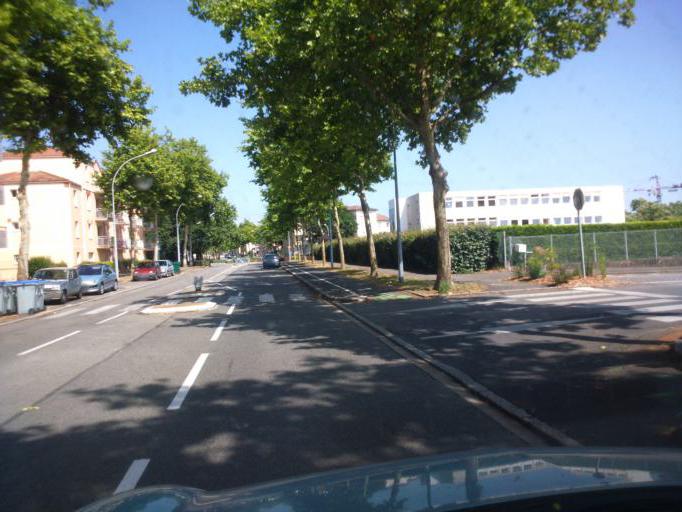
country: FR
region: Pays de la Loire
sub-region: Departement de la Loire-Atlantique
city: Saint-Sebastien-sur-Loire
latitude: 47.1991
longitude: -1.5273
